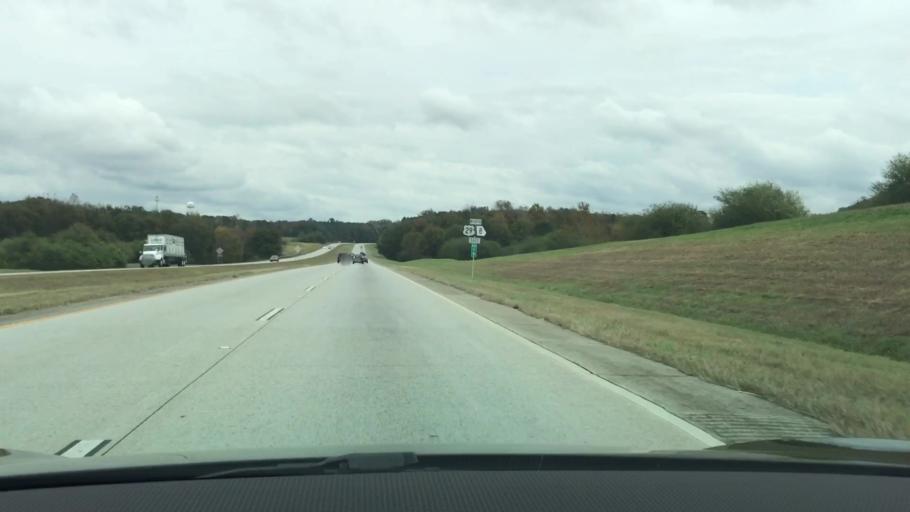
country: US
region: Georgia
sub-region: Barrow County
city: Statham
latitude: 33.9615
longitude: -83.6309
